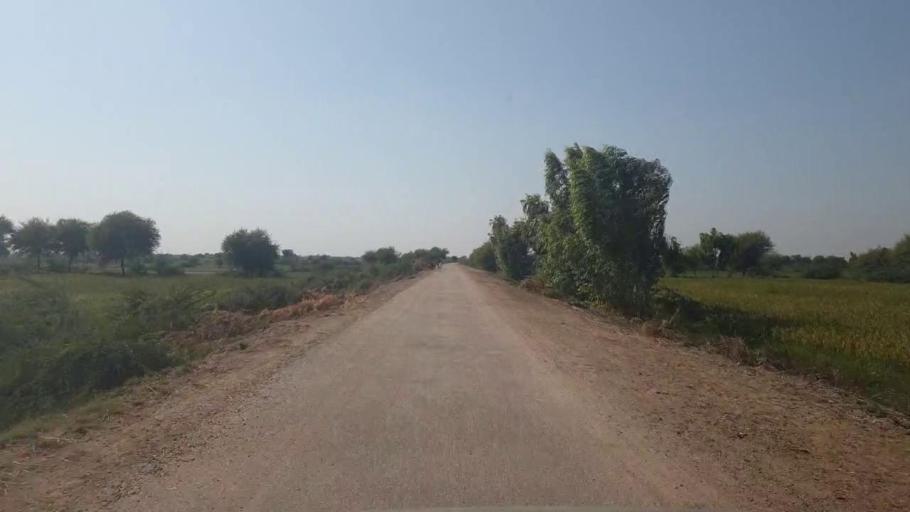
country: PK
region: Sindh
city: Badin
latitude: 24.5545
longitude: 68.8272
